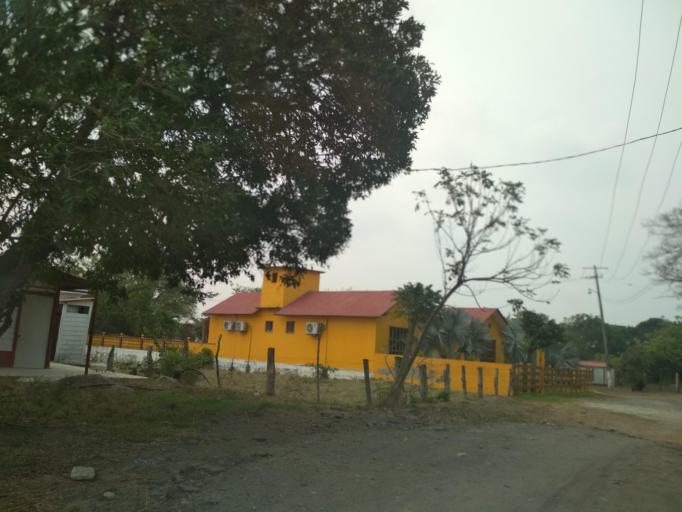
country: MX
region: Veracruz
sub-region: Veracruz
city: Fraccionamiento Geovillas los Pinos
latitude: 19.2106
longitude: -96.2468
